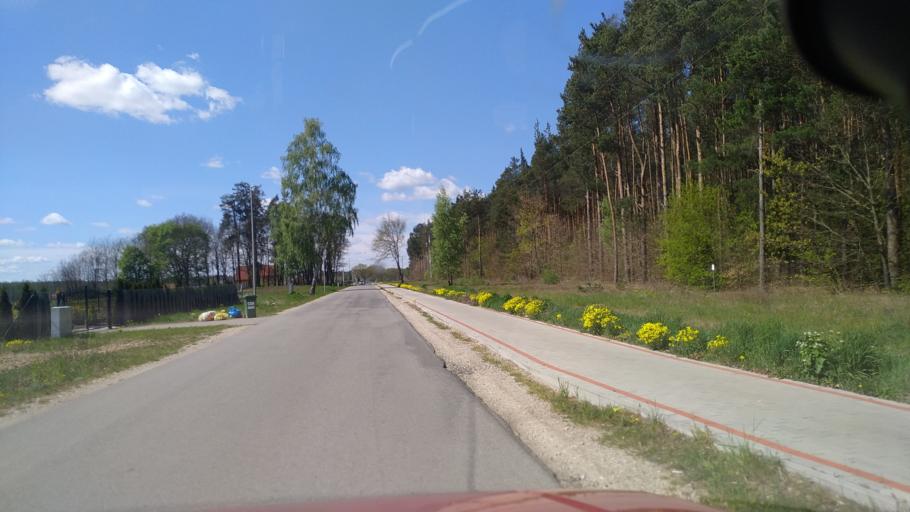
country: PL
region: Greater Poland Voivodeship
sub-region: Powiat zlotowski
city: Krajenka
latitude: 53.2642
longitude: 16.9144
